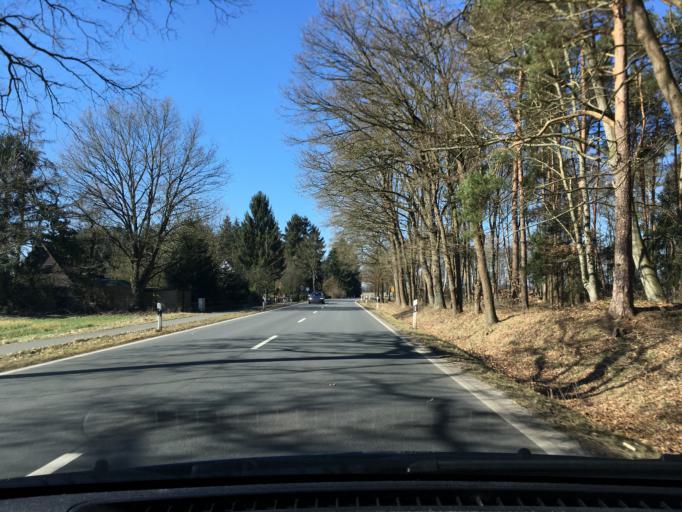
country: DE
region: Lower Saxony
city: Brockel
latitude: 53.0916
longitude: 9.5423
